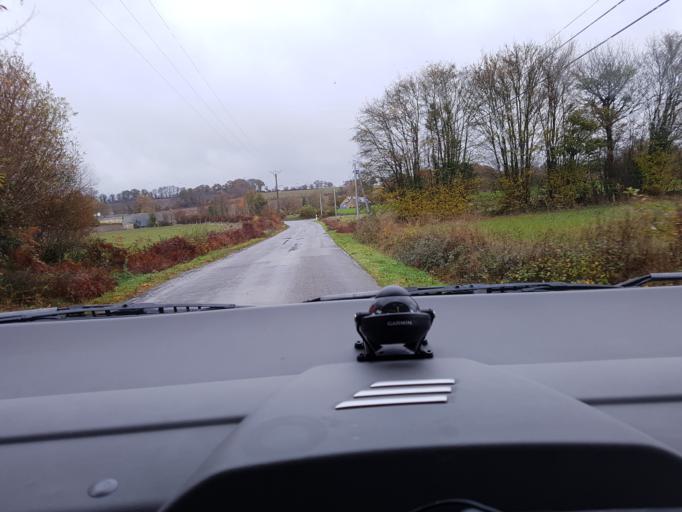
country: FR
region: Pays de la Loire
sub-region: Departement de la Mayenne
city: Montenay
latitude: 48.3088
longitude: -0.8681
